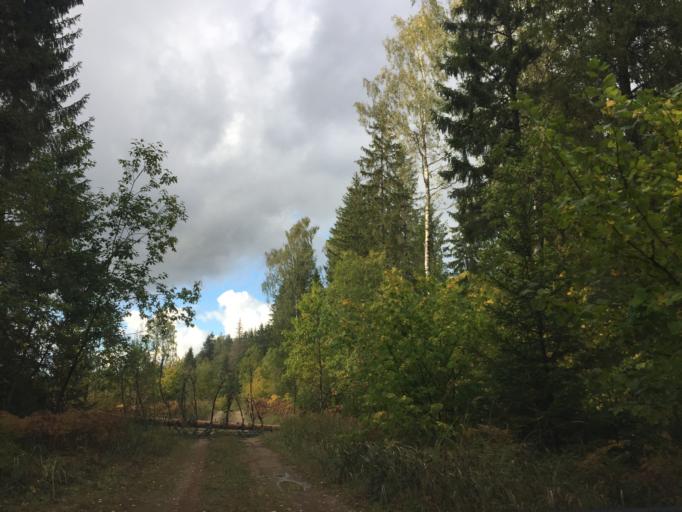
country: LV
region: Ligatne
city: Ligatne
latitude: 57.1051
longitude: 25.1463
